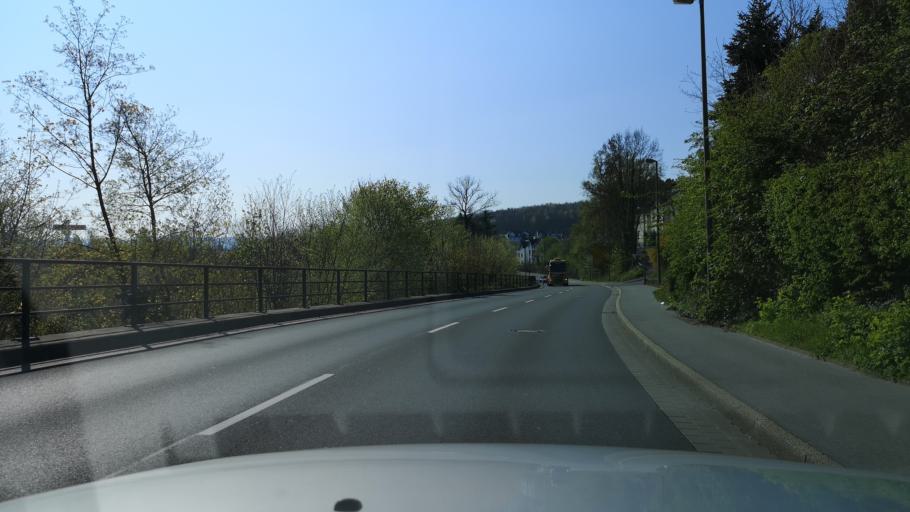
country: DE
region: North Rhine-Westphalia
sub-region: Regierungsbezirk Arnsberg
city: Menden
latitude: 51.4442
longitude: 7.7792
